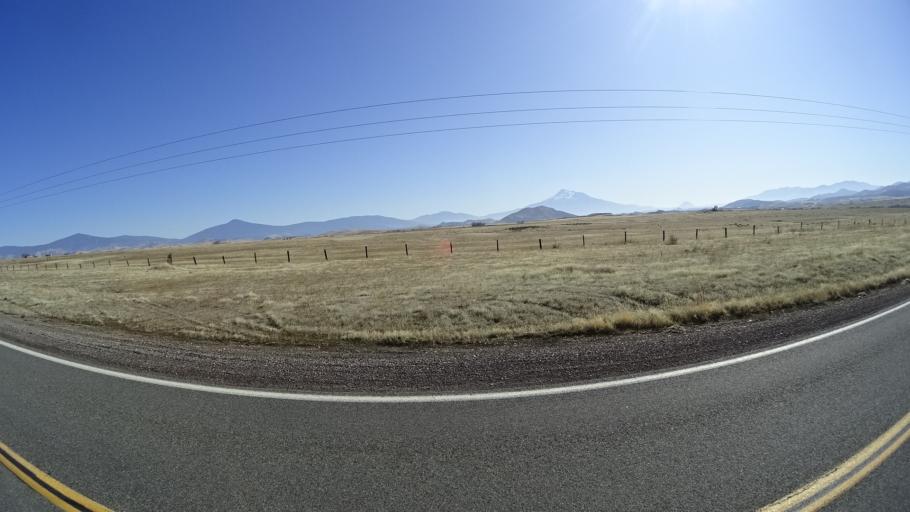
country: US
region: California
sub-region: Siskiyou County
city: Montague
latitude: 41.7564
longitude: -122.5666
